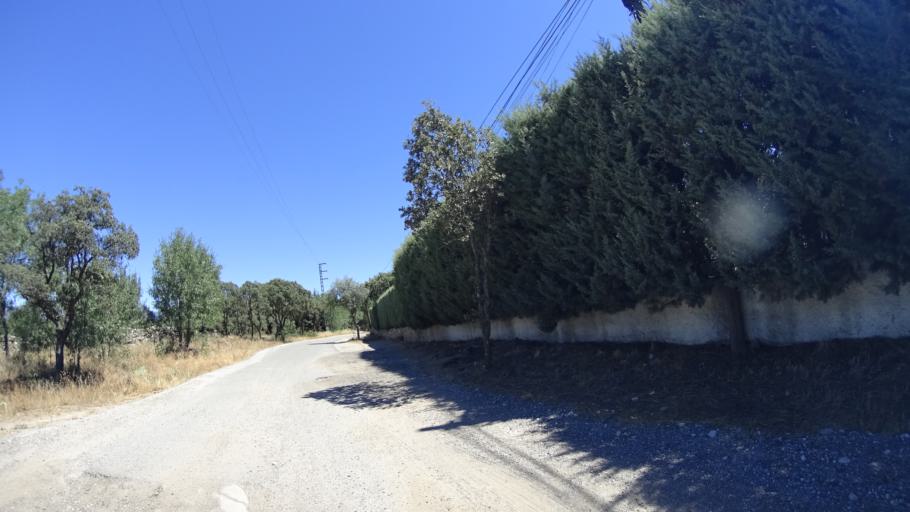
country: ES
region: Madrid
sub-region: Provincia de Madrid
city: Alpedrete
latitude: 40.6640
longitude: -4.0496
